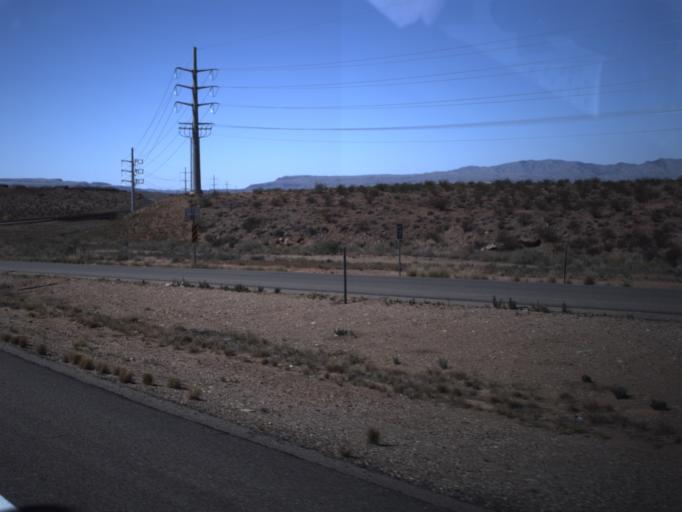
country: US
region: Utah
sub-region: Washington County
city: Washington
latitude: 37.0116
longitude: -113.4981
